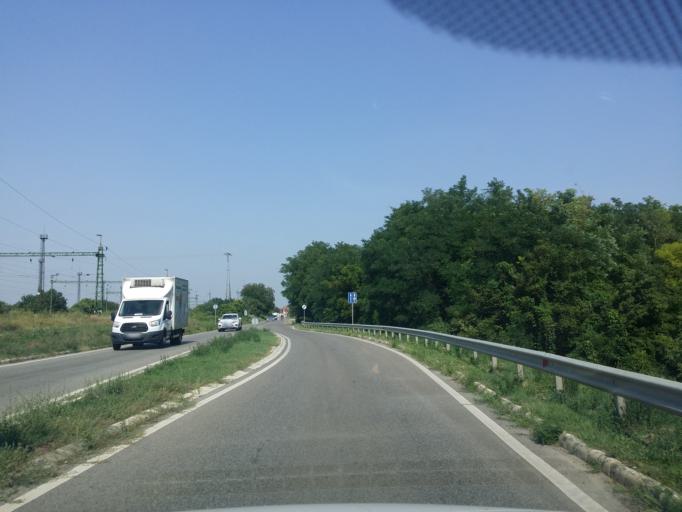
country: HU
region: Tolna
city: Simontornya
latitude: 46.7516
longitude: 18.5350
